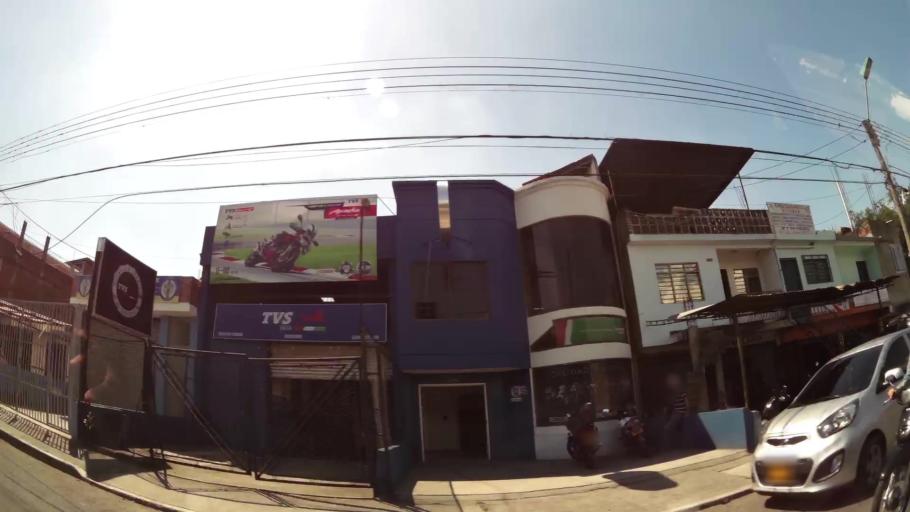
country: CO
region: Valle del Cauca
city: Cali
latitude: 3.4416
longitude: -76.4966
